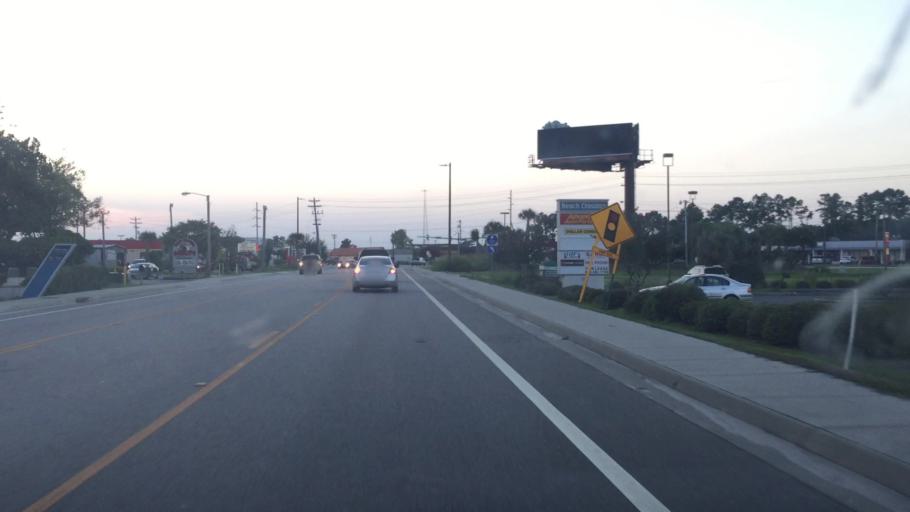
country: US
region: South Carolina
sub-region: Horry County
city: Myrtle Beach
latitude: 33.6974
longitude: -78.8988
